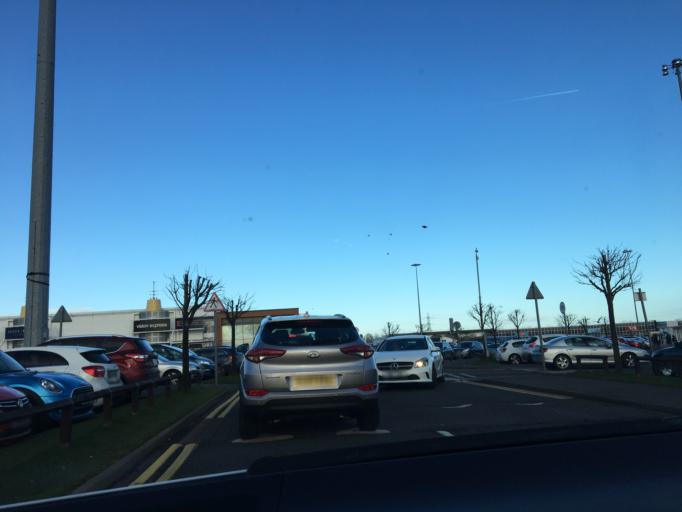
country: GB
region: Scotland
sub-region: West Lothian
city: Seafield
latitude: 55.9337
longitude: -3.1057
